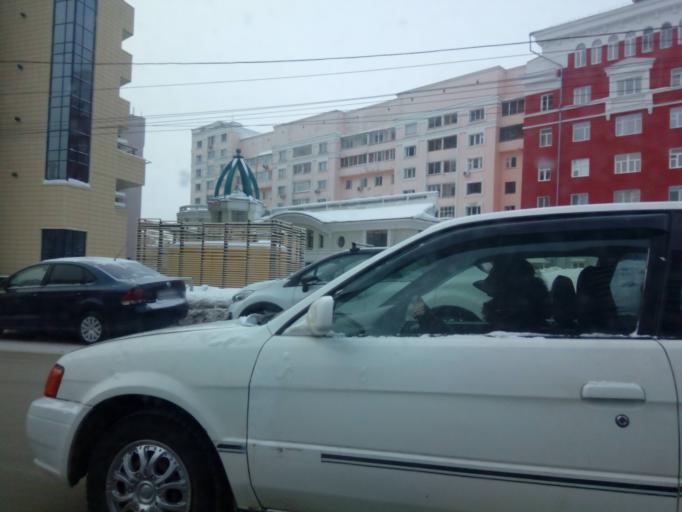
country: RU
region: Novosibirsk
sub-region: Novosibirskiy Rayon
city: Novosibirsk
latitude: 55.0298
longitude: 82.9079
